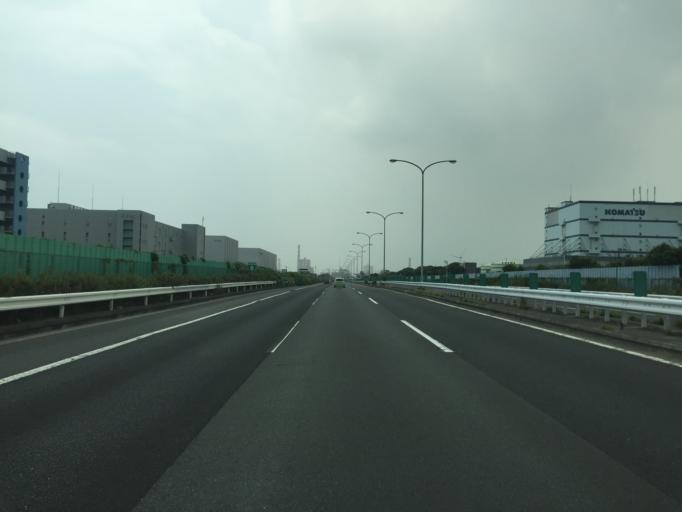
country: JP
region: Kanagawa
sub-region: Kawasaki-shi
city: Kawasaki
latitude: 35.4950
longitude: 139.7515
